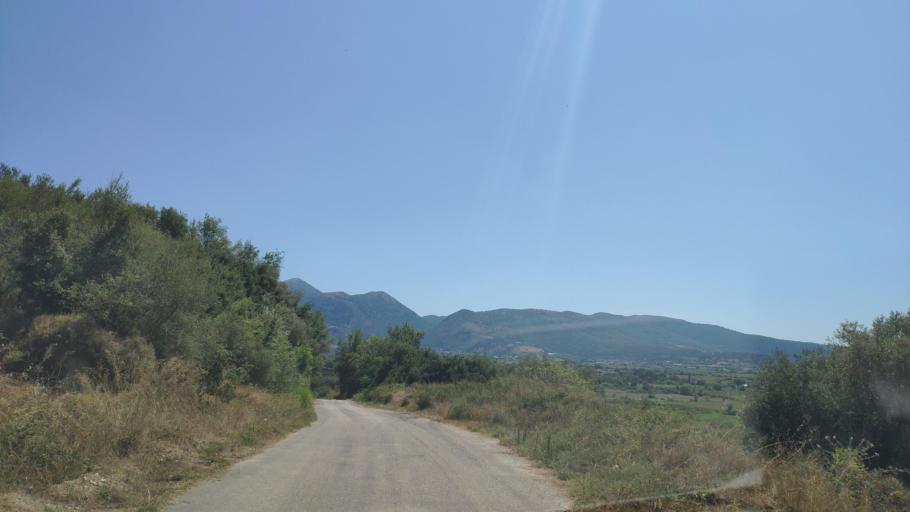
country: GR
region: Epirus
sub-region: Nomos Prevezis
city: Kanalaki
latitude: 39.2719
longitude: 20.6001
